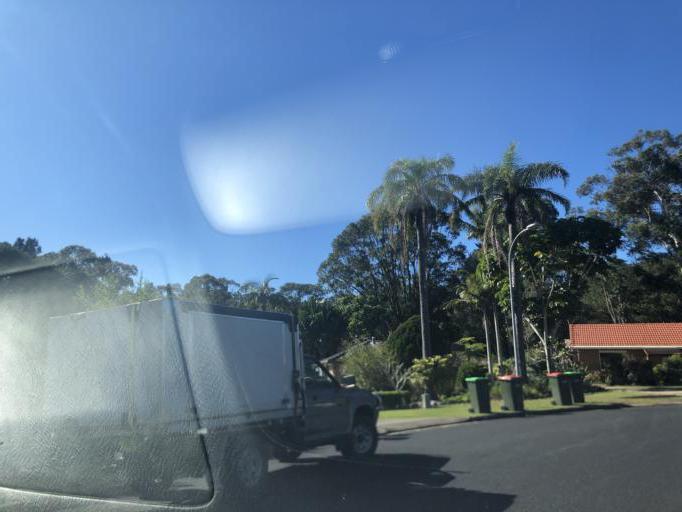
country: AU
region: New South Wales
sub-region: Coffs Harbour
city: Toormina
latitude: -30.3680
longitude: 153.0856
